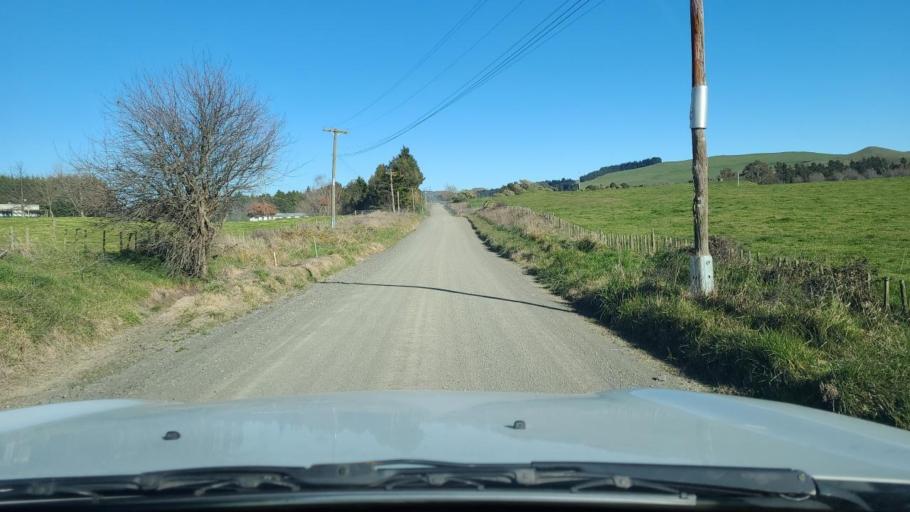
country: NZ
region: Hawke's Bay
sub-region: Napier City
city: Taradale
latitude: -39.3898
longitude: 176.5504
